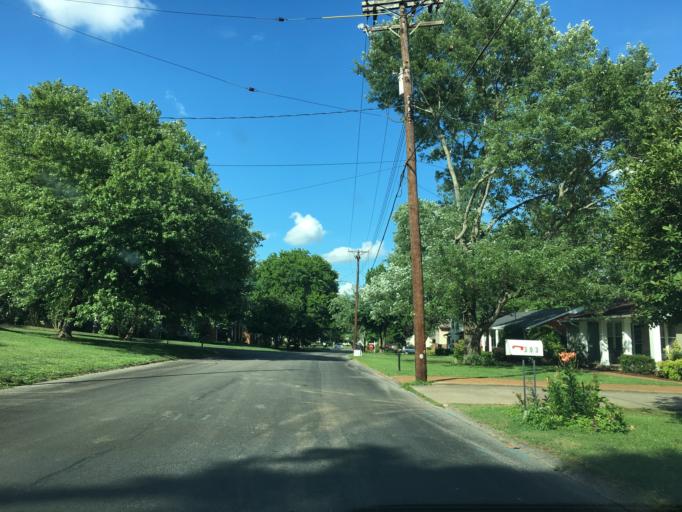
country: US
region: Tennessee
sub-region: Davidson County
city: Oak Hill
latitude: 36.0901
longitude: -86.7231
